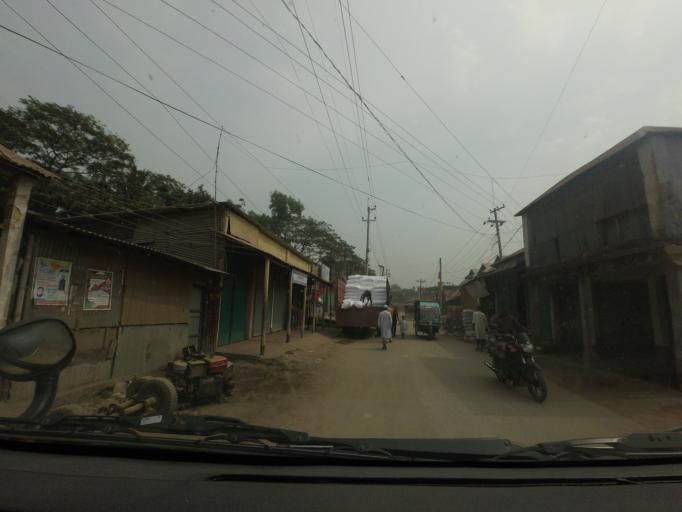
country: BD
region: Dhaka
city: Kishorganj
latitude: 24.3406
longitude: 90.7958
